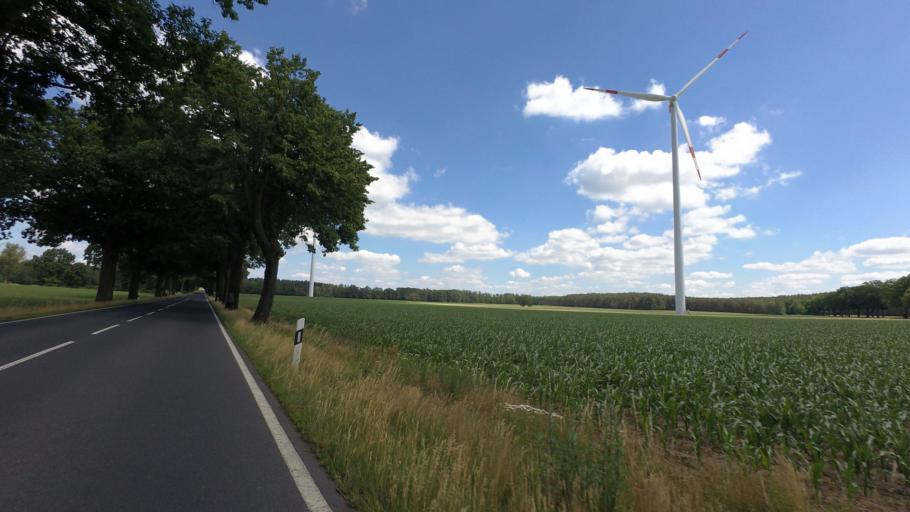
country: DE
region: Brandenburg
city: Sonnewalde
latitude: 51.7192
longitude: 13.6723
